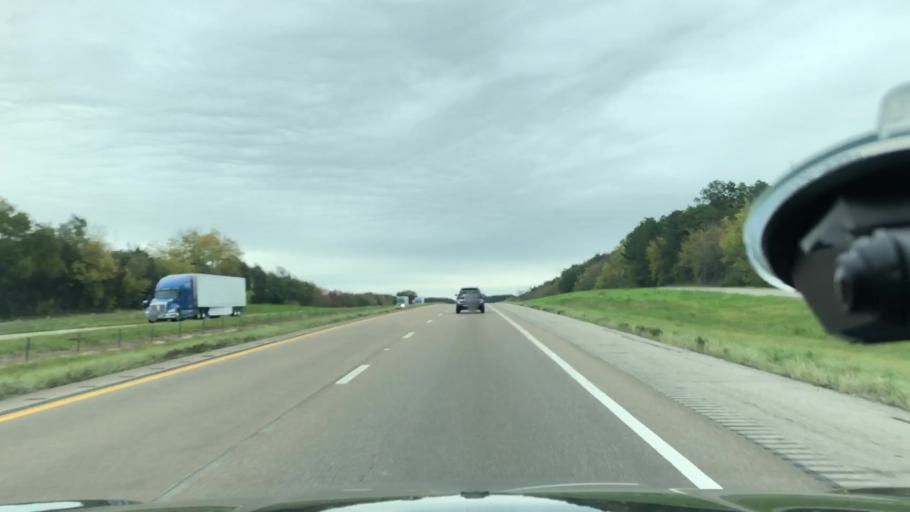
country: US
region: Texas
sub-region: Titus County
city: Mount Pleasant
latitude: 33.1596
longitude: -95.0897
